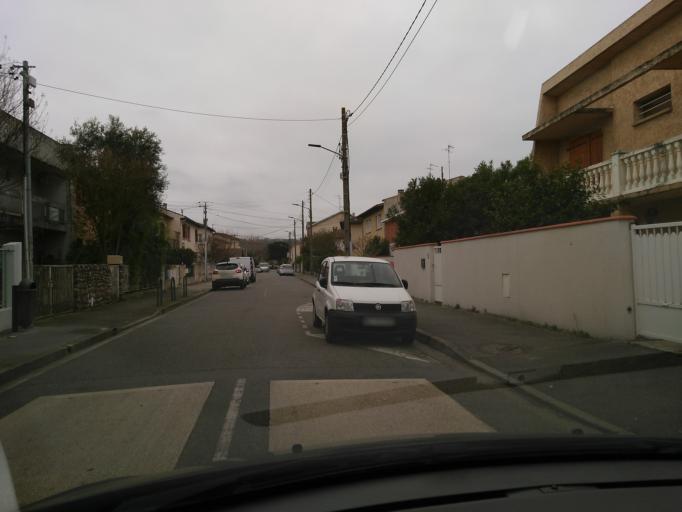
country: FR
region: Midi-Pyrenees
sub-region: Departement de la Haute-Garonne
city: Toulouse
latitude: 43.5782
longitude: 1.4612
